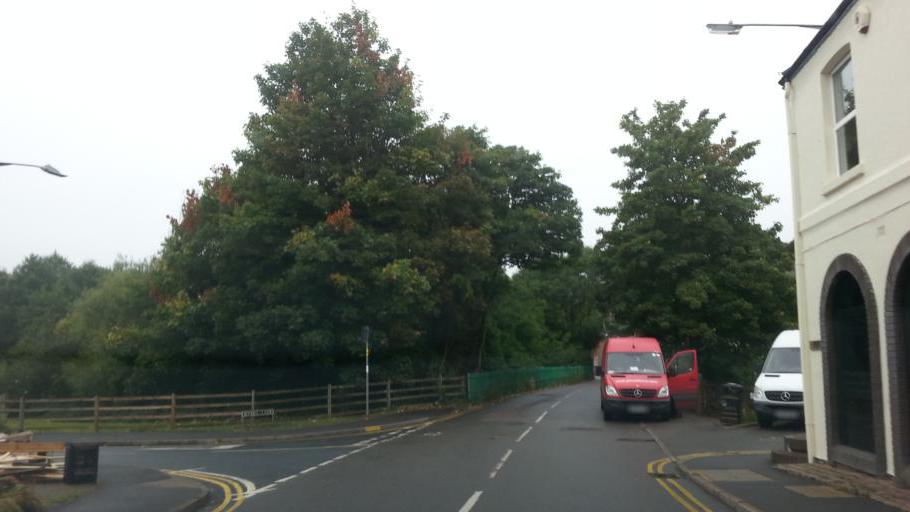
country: GB
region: England
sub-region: Warwickshire
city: Kenilworth
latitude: 52.3509
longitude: -1.5732
